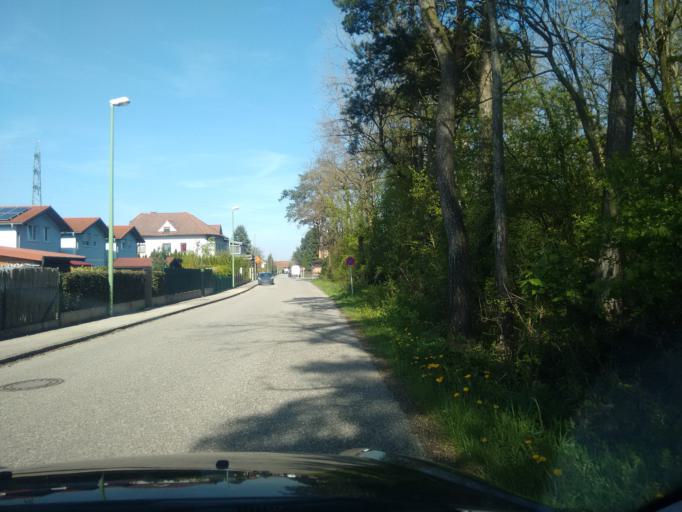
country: AT
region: Upper Austria
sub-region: Wels-Land
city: Holzhausen
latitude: 48.1946
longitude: 14.0679
